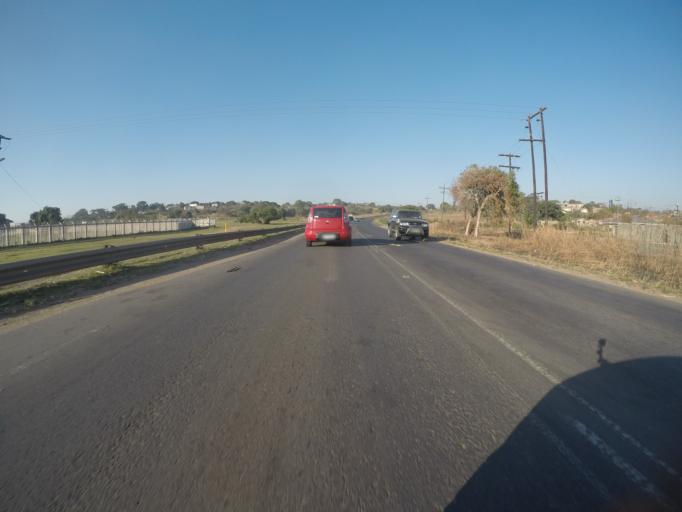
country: ZA
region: KwaZulu-Natal
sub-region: iLembe District Municipality
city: Stanger
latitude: -29.3992
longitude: 31.2521
